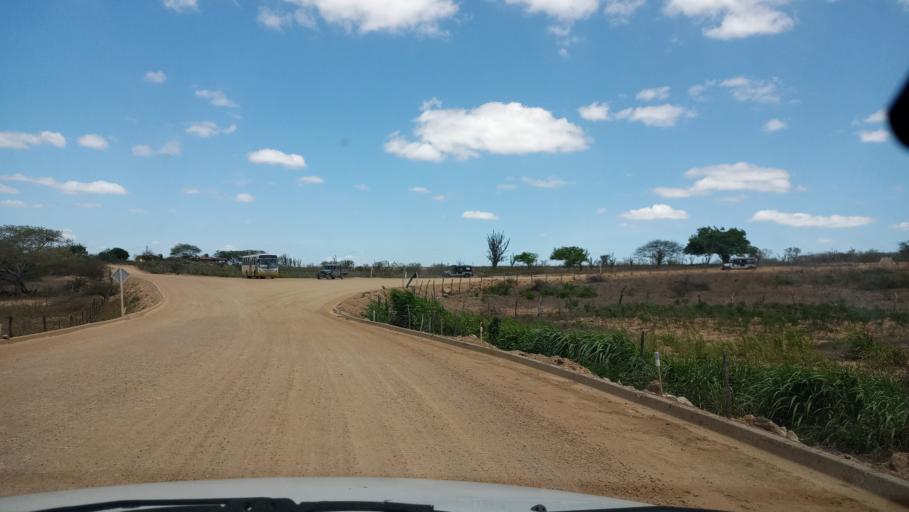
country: BR
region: Rio Grande do Norte
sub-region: Sao Paulo Do Potengi
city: Sao Paulo do Potengi
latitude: -5.7881
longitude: -35.9160
